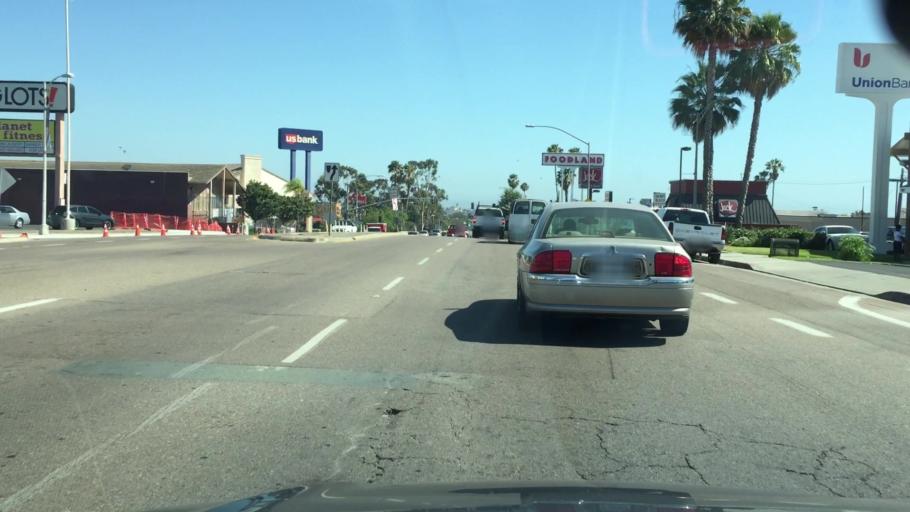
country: US
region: California
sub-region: San Diego County
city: National City
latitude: 32.7229
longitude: -117.0850
